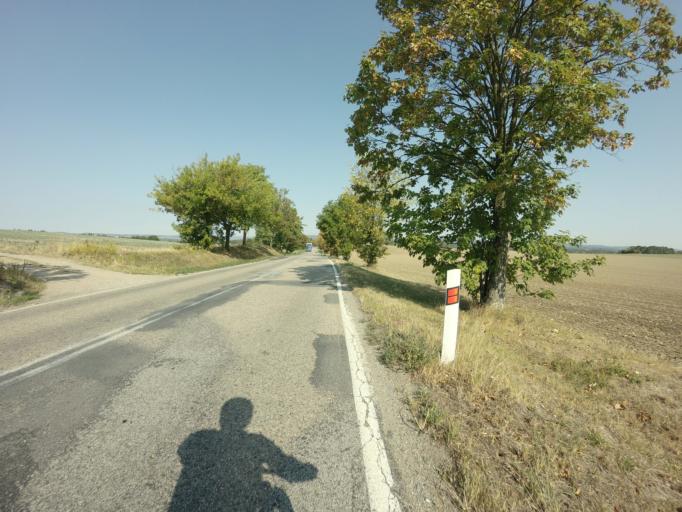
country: CZ
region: Central Bohemia
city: Porici nad Sazavou
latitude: 49.8164
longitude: 14.6397
